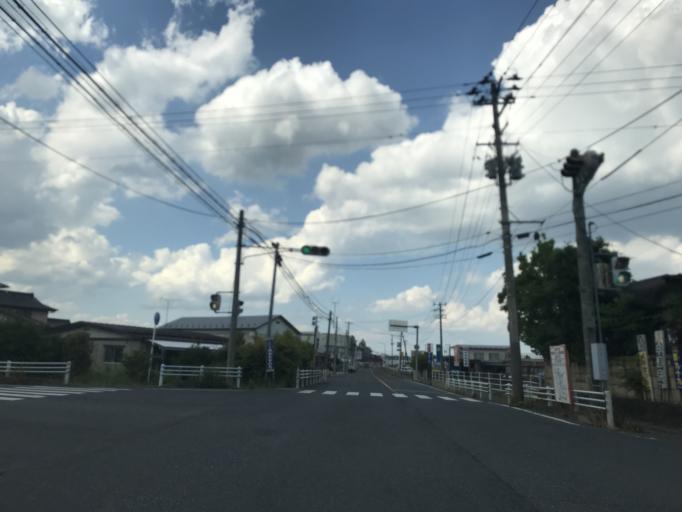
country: JP
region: Miyagi
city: Wakuya
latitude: 38.6147
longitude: 141.1784
